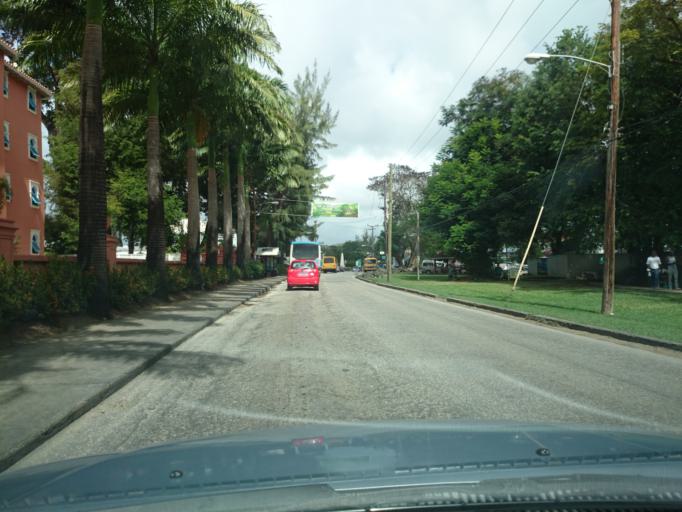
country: BB
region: Saint James
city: Holetown
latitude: 13.1843
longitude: -59.6384
